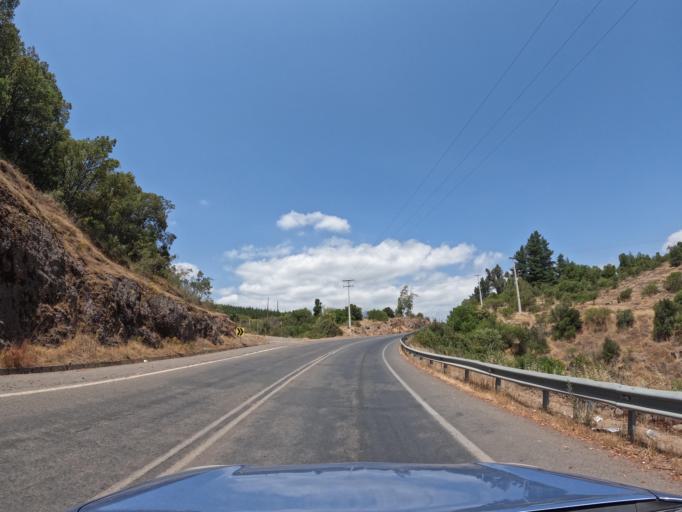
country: CL
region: Maule
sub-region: Provincia de Curico
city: Molina
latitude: -35.1812
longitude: -71.1149
